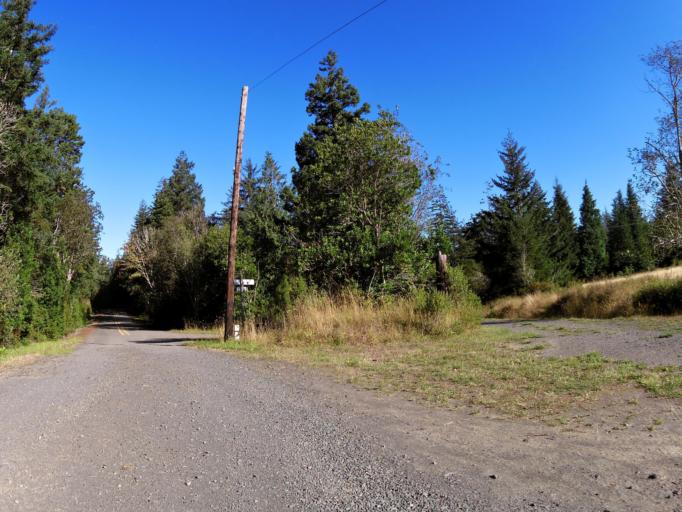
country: US
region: Oregon
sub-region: Coos County
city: Bandon
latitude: 43.0352
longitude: -124.3908
